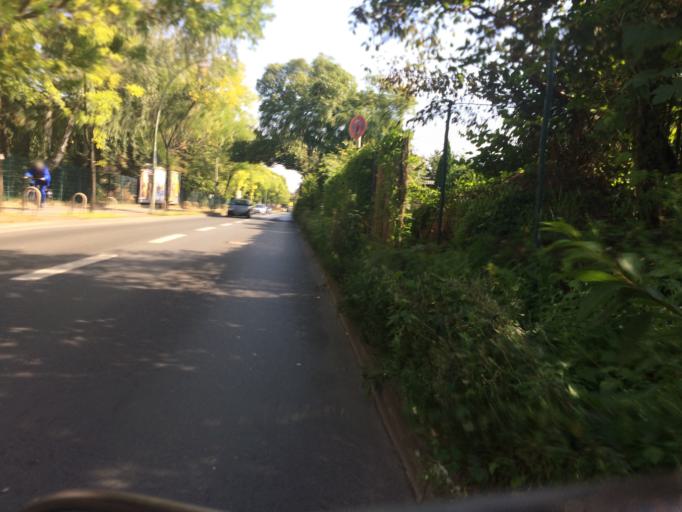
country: DE
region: Berlin
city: Heinersdorf
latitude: 52.5713
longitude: 13.4315
